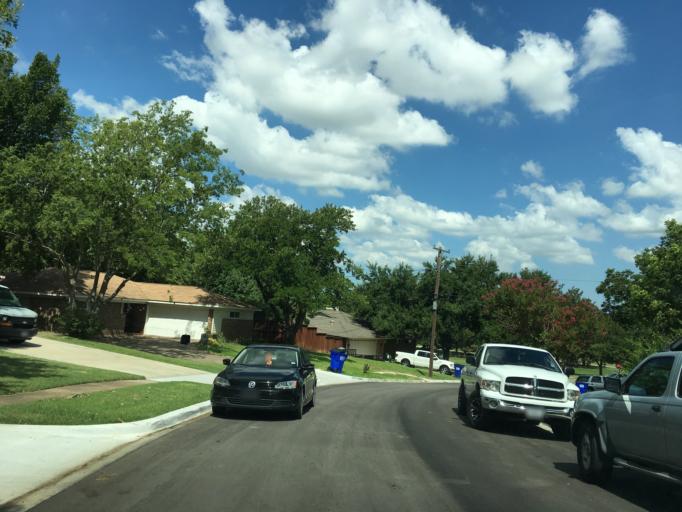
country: US
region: Texas
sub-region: Dallas County
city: Farmers Branch
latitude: 32.9291
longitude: -96.8781
